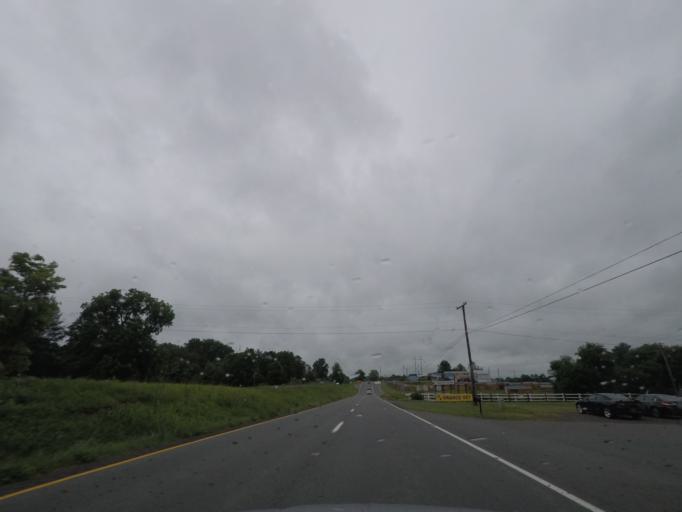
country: US
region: Virginia
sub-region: Orange County
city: Orange
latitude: 38.2195
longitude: -78.1266
